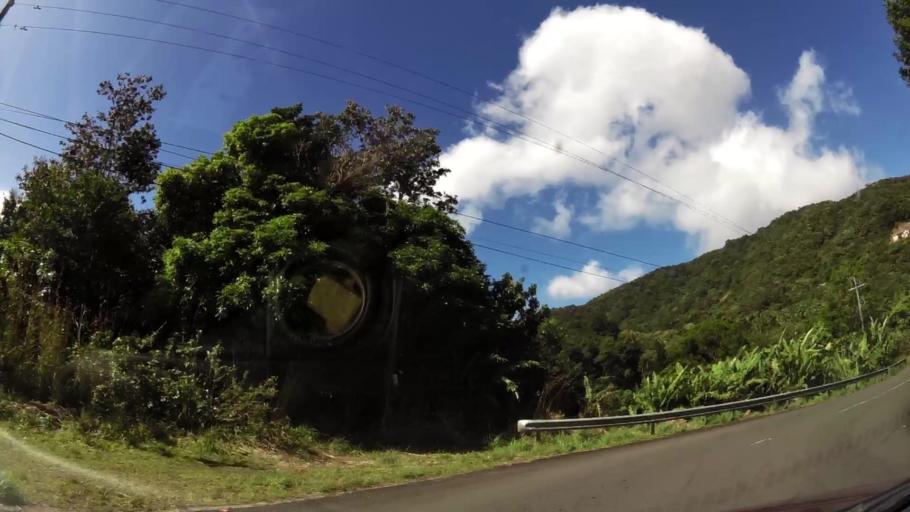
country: DM
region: Saint Paul
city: Pont Casse
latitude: 15.3510
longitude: -61.3603
